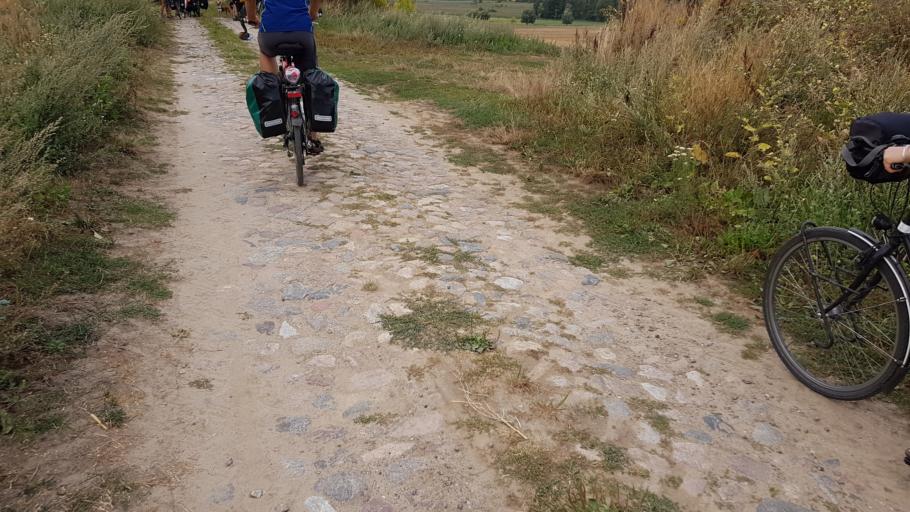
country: PL
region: West Pomeranian Voivodeship
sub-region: Powiat mysliborski
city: Barlinek
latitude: 53.0761
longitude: 15.2036
